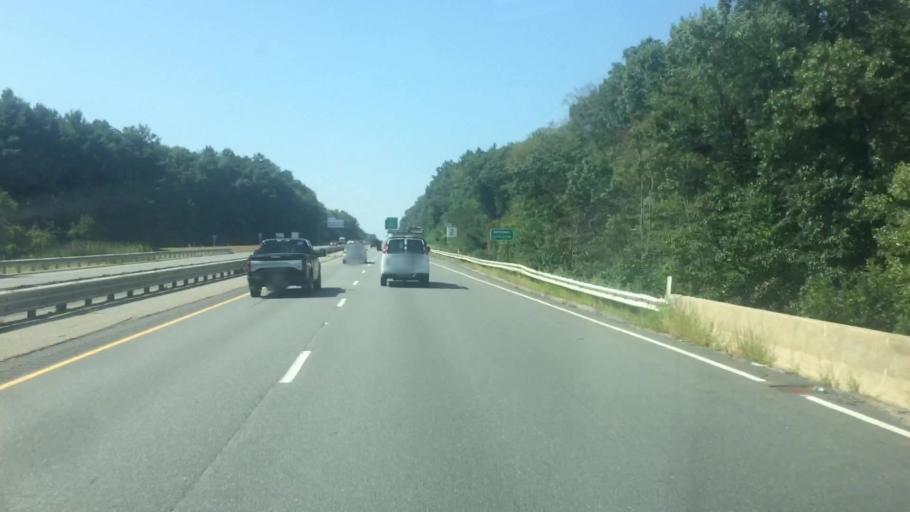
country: US
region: Massachusetts
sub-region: Middlesex County
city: Littleton Common
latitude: 42.5007
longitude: -71.4754
